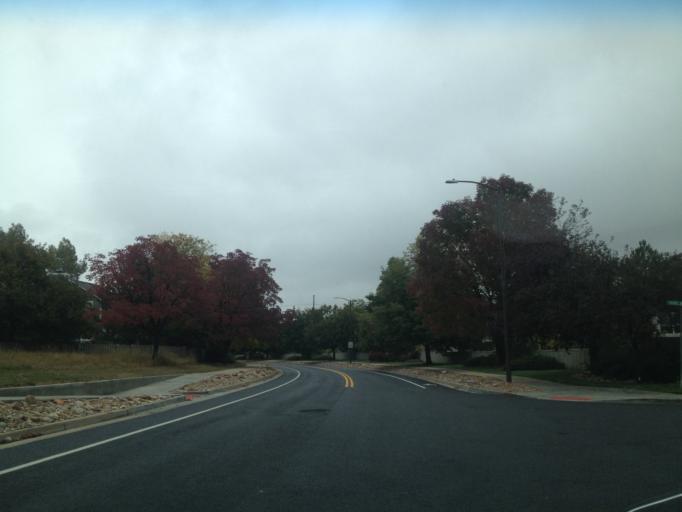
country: US
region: Colorado
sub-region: Boulder County
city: Superior
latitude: 39.9776
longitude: -105.1592
